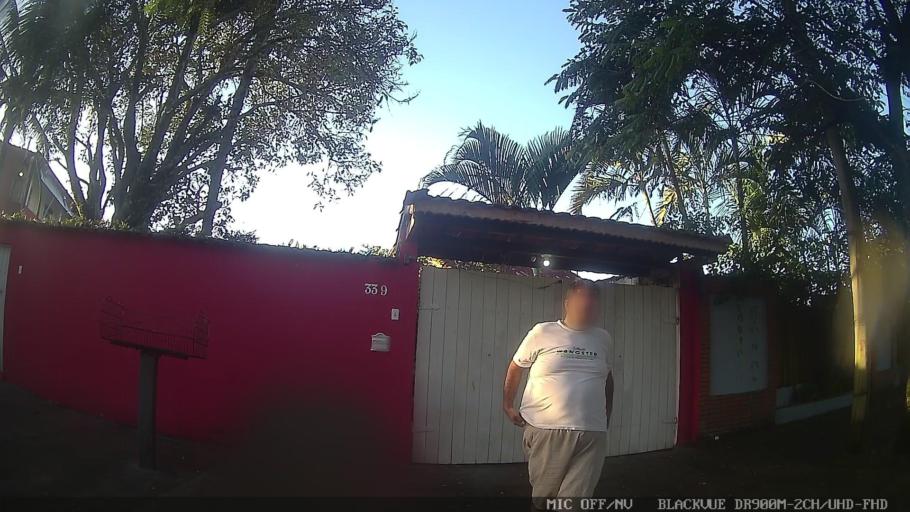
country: BR
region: Sao Paulo
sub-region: Itanhaem
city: Itanhaem
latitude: -24.2343
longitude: -46.8802
